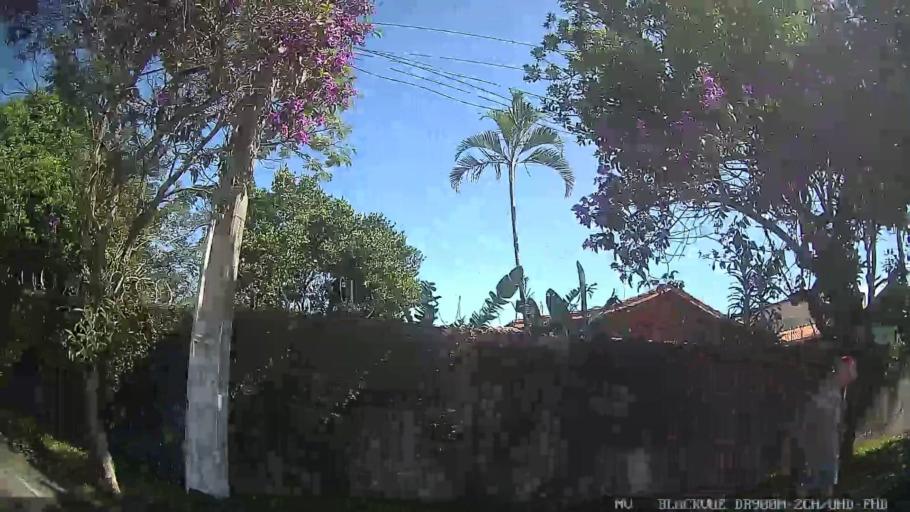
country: BR
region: Sao Paulo
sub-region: Atibaia
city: Atibaia
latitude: -23.1160
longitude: -46.5954
